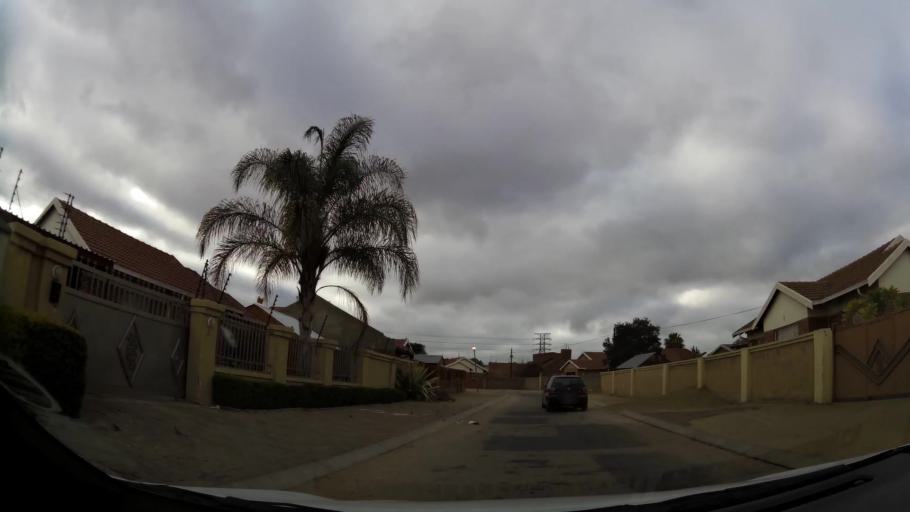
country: ZA
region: Limpopo
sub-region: Capricorn District Municipality
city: Polokwane
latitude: -23.9209
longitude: 29.4494
